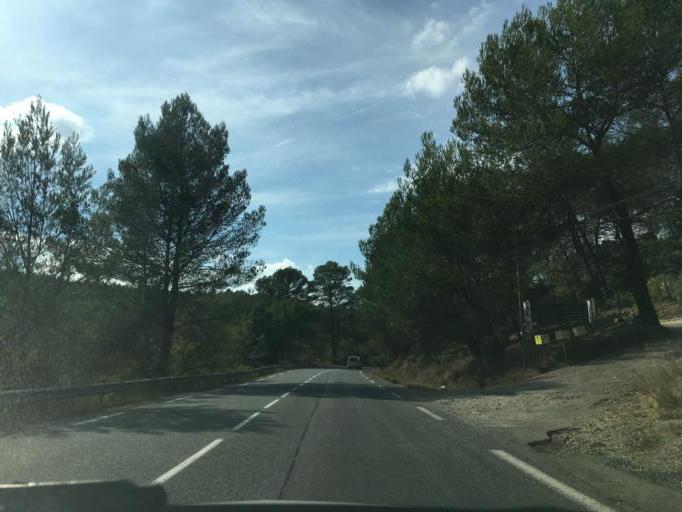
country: FR
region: Provence-Alpes-Cote d'Azur
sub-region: Departement du Var
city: Flayosc
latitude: 43.5428
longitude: 6.3545
